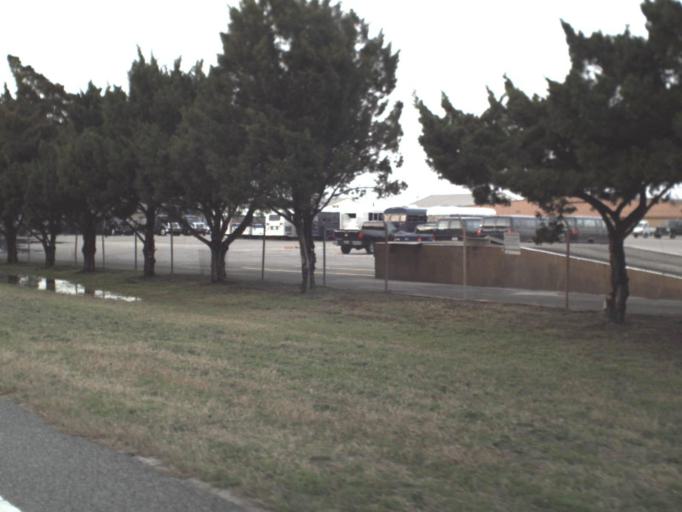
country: US
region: Florida
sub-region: Bay County
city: Tyndall Air Force Base
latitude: 30.0680
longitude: -85.5877
